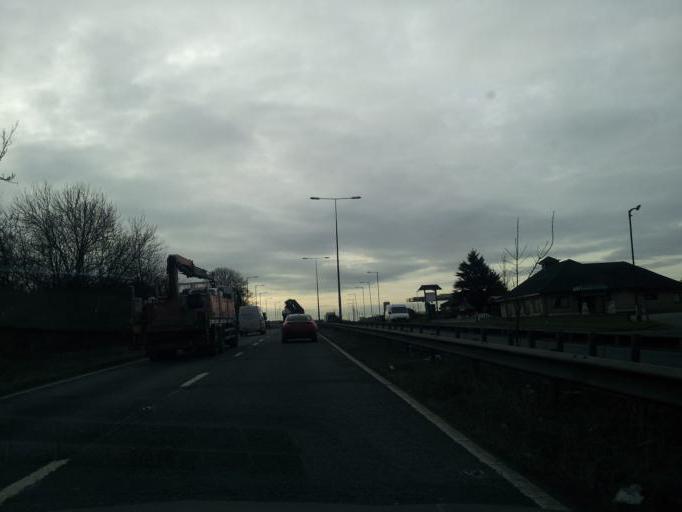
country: GB
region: England
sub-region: District of Rutland
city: Clipsham
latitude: 52.8076
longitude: -0.6135
